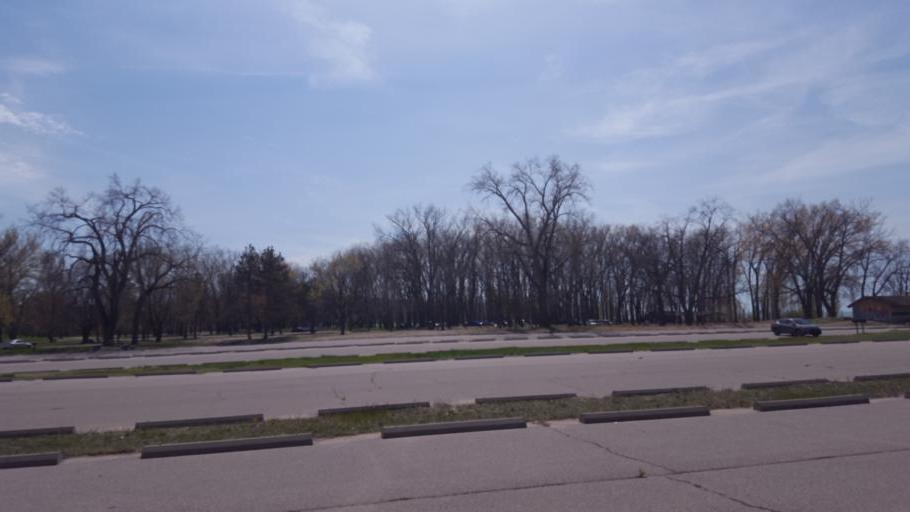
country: US
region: Ohio
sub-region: Lake County
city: Fairport Harbor
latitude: 41.7570
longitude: -81.2871
